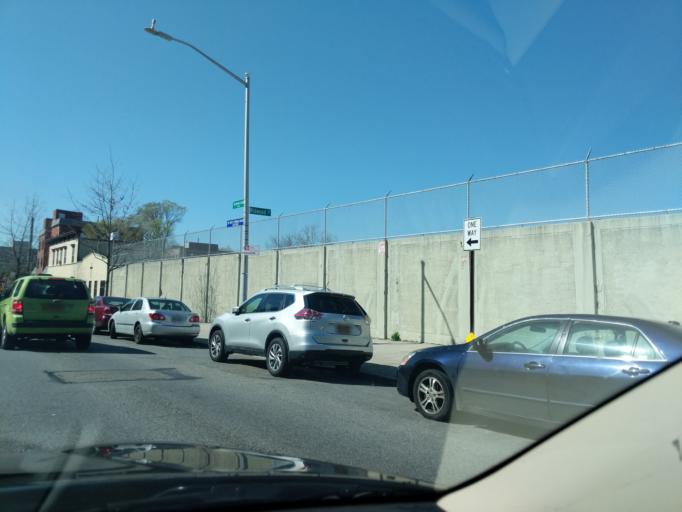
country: US
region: New York
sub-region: Kings County
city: Brooklyn
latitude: 40.6612
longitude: -73.9343
